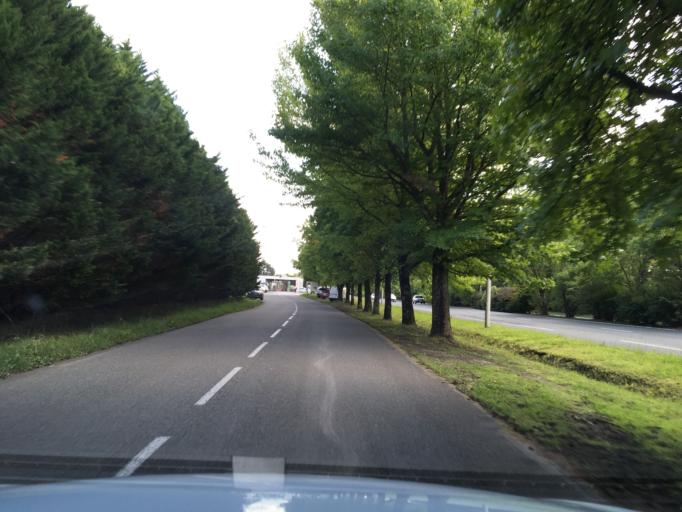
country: FR
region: Aquitaine
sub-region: Departement des Pyrenees-Atlantiques
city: Bayonne
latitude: 43.4818
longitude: -1.4912
